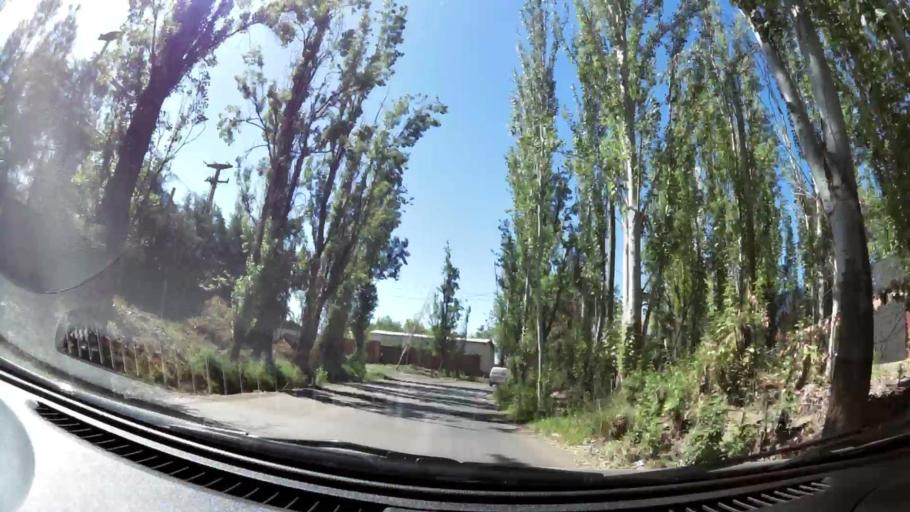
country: AR
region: Mendoza
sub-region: Departamento de Godoy Cruz
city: Godoy Cruz
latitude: -32.9776
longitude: -68.8415
